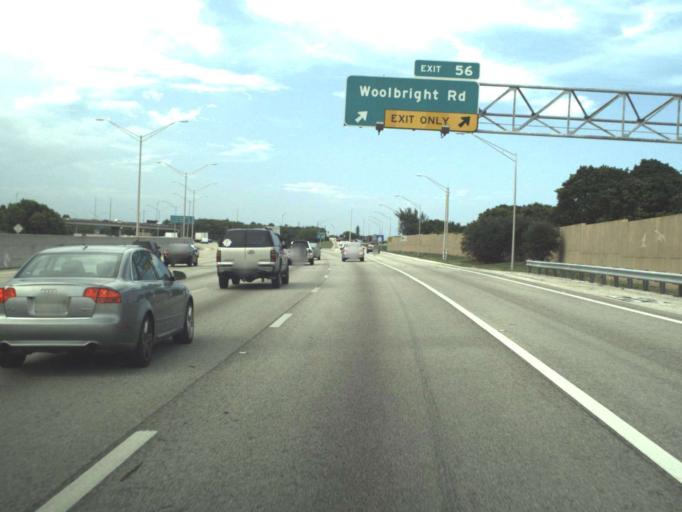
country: US
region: Florida
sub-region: Palm Beach County
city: Boynton Beach
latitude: 26.5098
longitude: -80.0731
